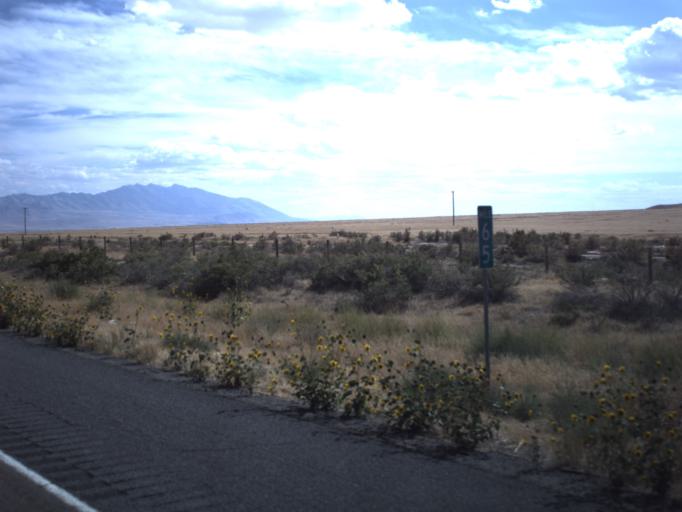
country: US
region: Utah
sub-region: Tooele County
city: Grantsville
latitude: 40.8012
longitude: -112.8518
